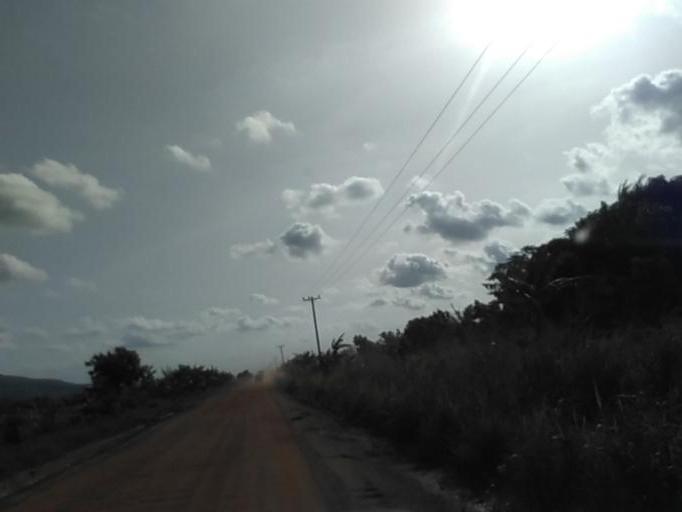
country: GH
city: Akropong
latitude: 6.0957
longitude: 0.2428
